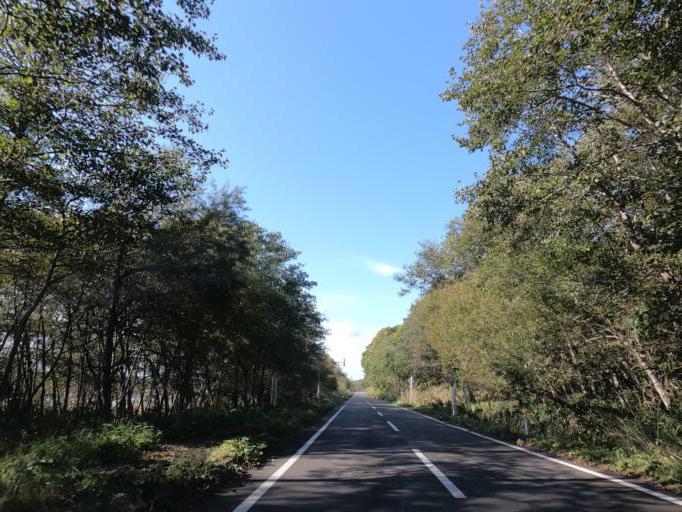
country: JP
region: Hokkaido
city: Obihiro
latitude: 42.6185
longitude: 143.5421
